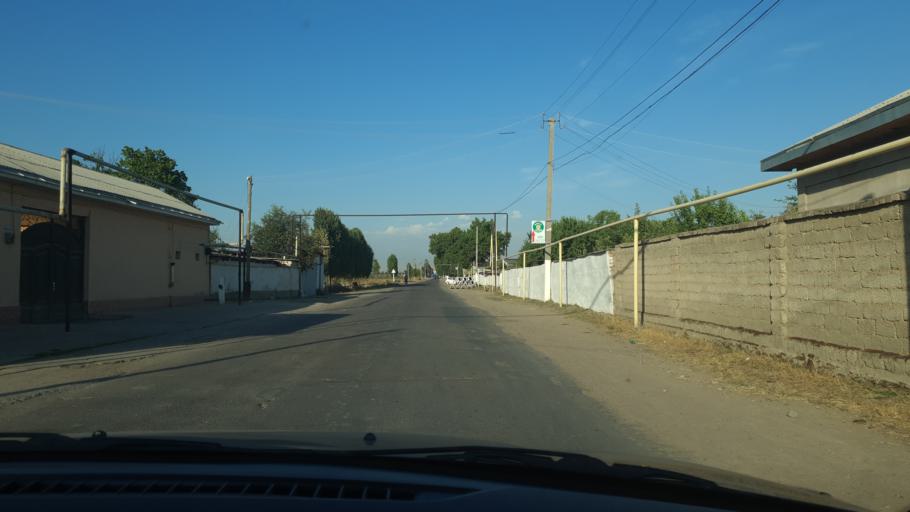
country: UZ
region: Toshkent
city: Tuytepa
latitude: 41.0843
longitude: 69.3329
